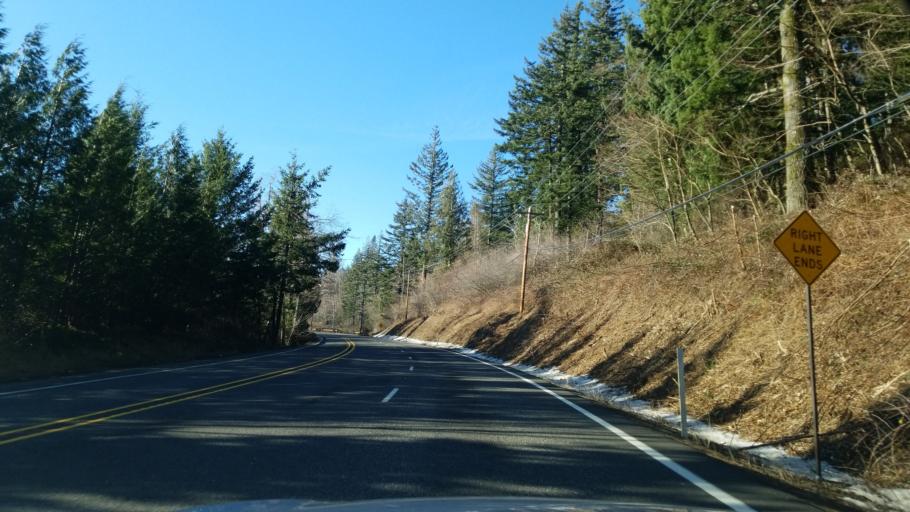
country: US
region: Washington
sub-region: Clark County
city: Washougal
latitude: 45.5914
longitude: -122.1543
